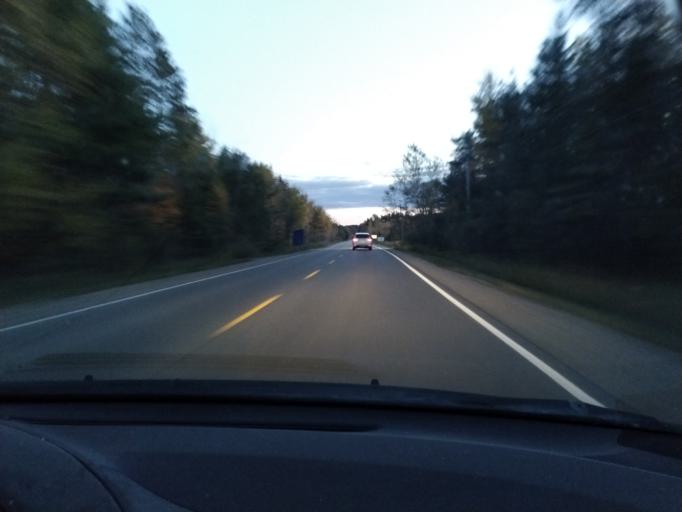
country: CA
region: Ontario
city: Bradford West Gwillimbury
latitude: 44.1780
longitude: -79.6591
